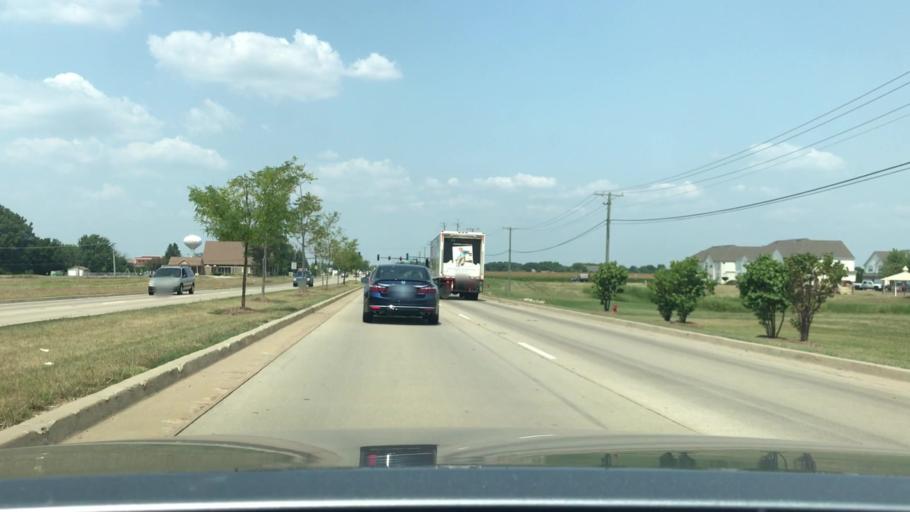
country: US
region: Illinois
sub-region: Will County
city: Plainfield
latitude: 41.5844
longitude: -88.2012
